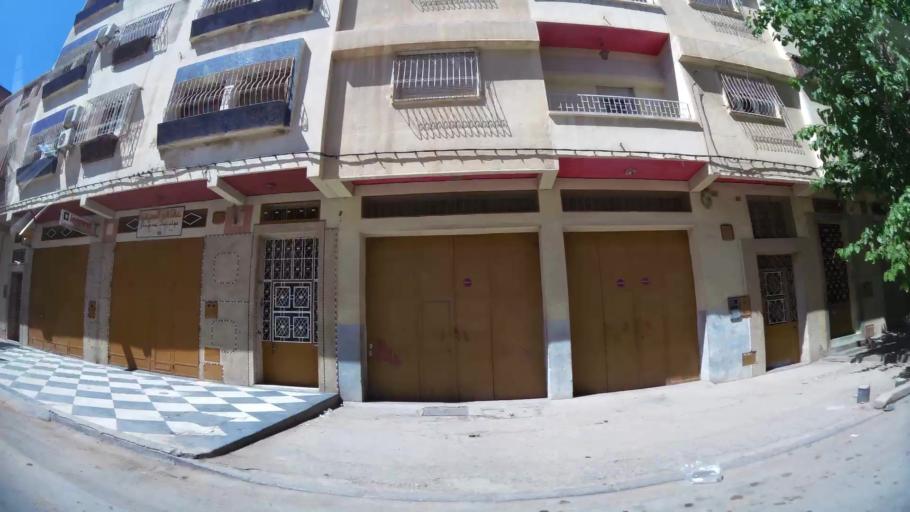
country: MA
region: Oriental
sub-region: Oujda-Angad
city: Oujda
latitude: 34.6701
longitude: -1.9339
